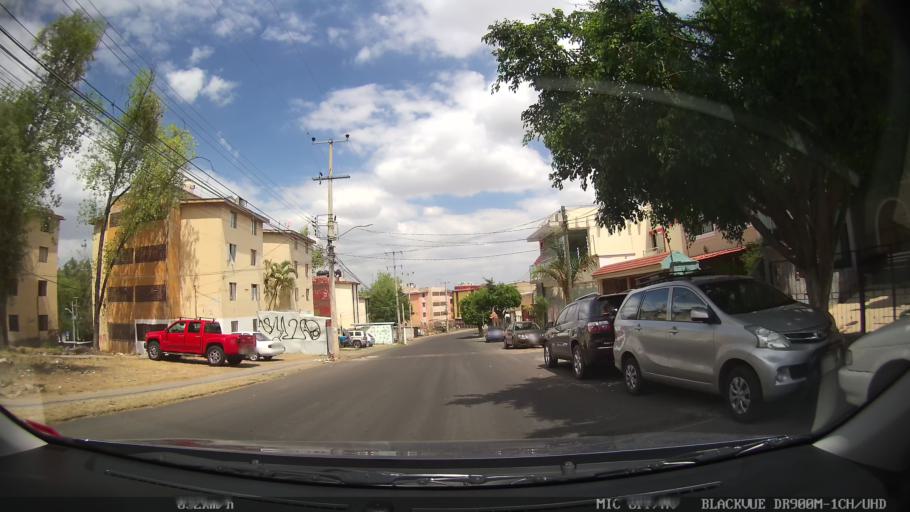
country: MX
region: Jalisco
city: Tonala
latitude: 20.6270
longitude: -103.2522
